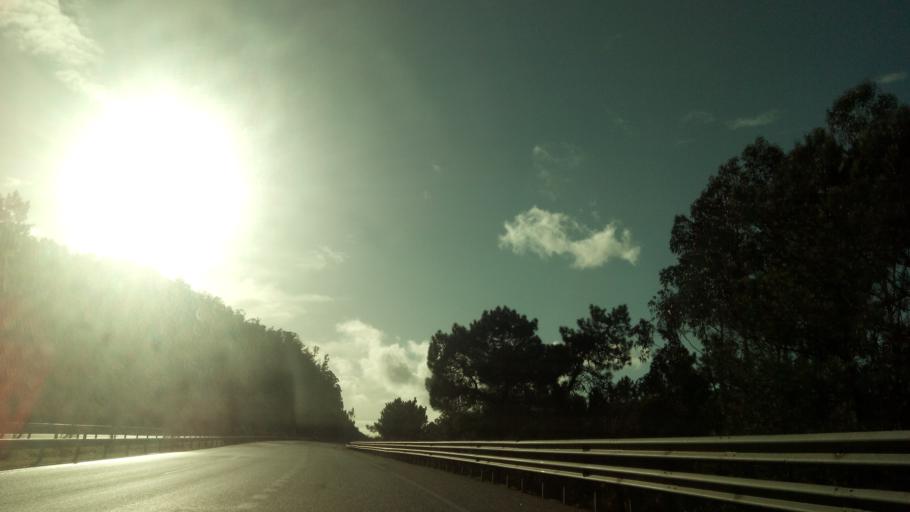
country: ES
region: Galicia
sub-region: Provincia de Pontevedra
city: Porrino
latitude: 42.1768
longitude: -8.5708
